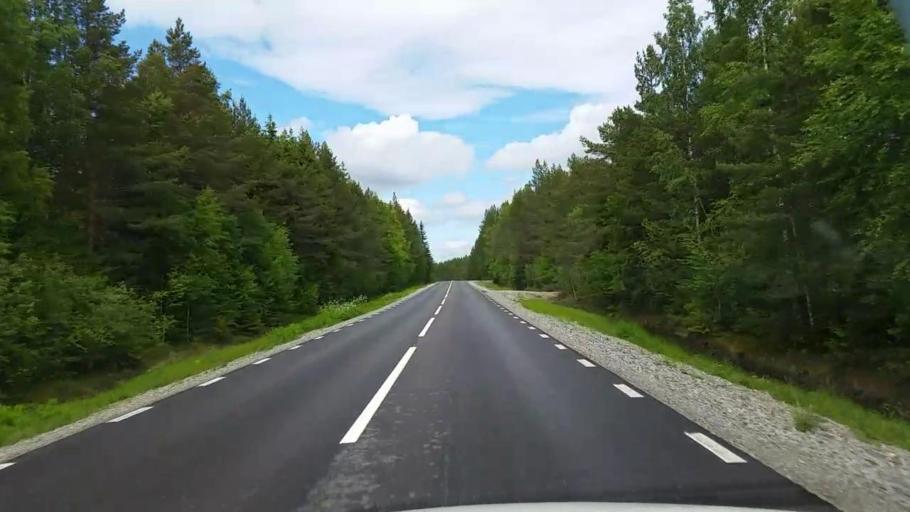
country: SE
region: Gaevleborg
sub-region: Sandvikens Kommun
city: Jarbo
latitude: 60.9127
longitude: 16.3746
